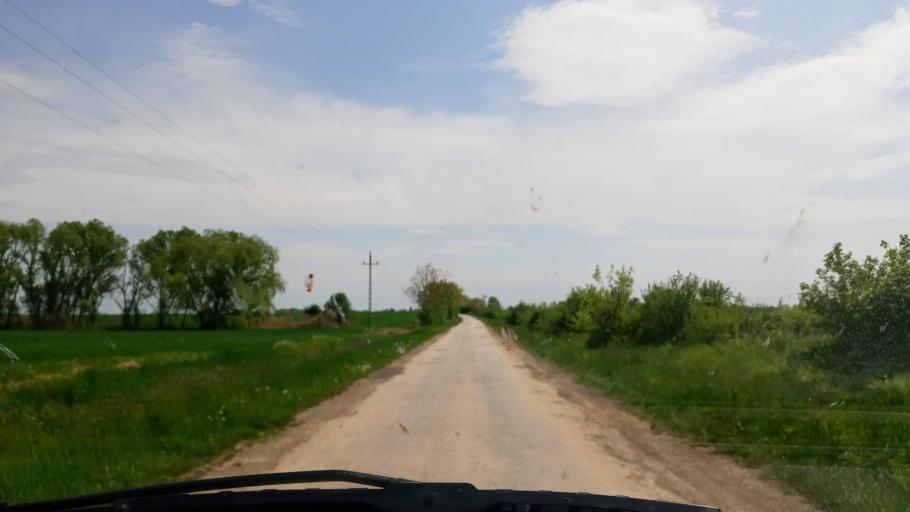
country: HU
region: Baranya
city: Villany
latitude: 45.8200
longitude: 18.5070
